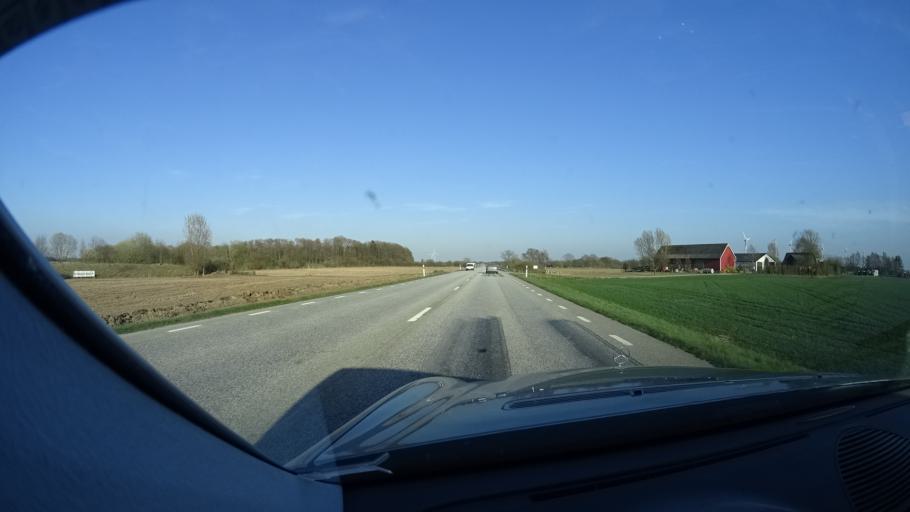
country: SE
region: Skane
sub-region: Eslovs Kommun
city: Stehag
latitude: 55.8499
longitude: 13.4235
